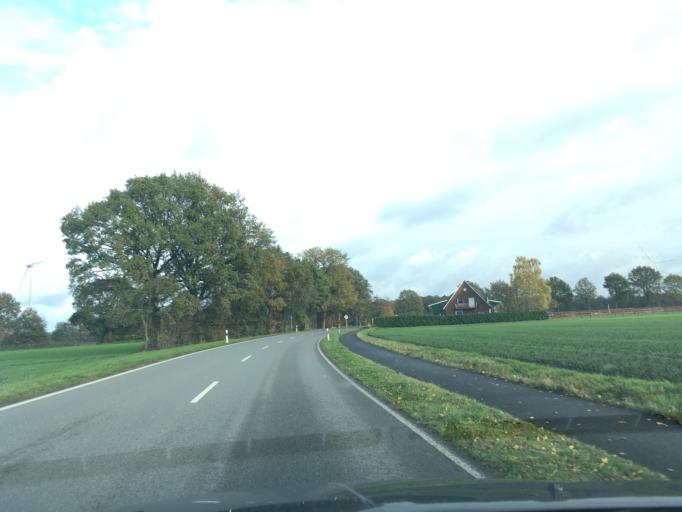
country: DE
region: North Rhine-Westphalia
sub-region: Regierungsbezirk Munster
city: Vreden
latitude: 52.0877
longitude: 6.8036
